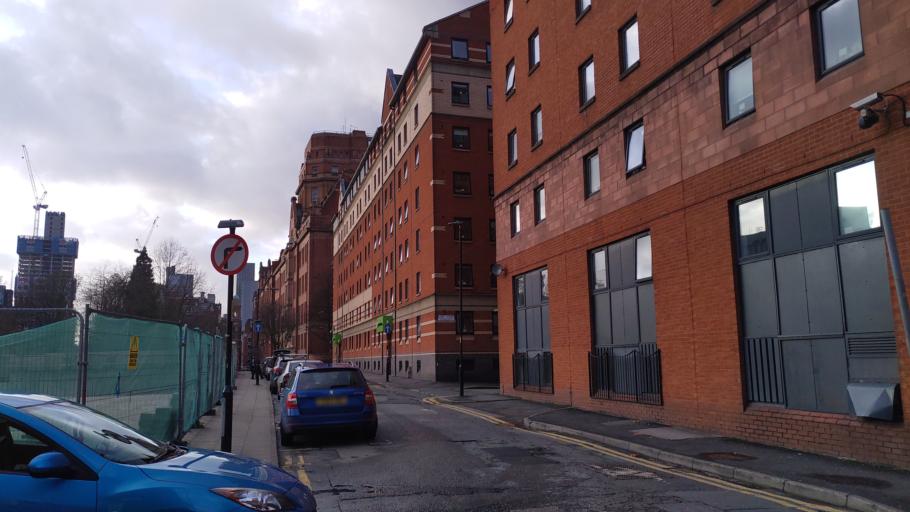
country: GB
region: England
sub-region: Manchester
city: Manchester
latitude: 53.4762
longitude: -2.2319
